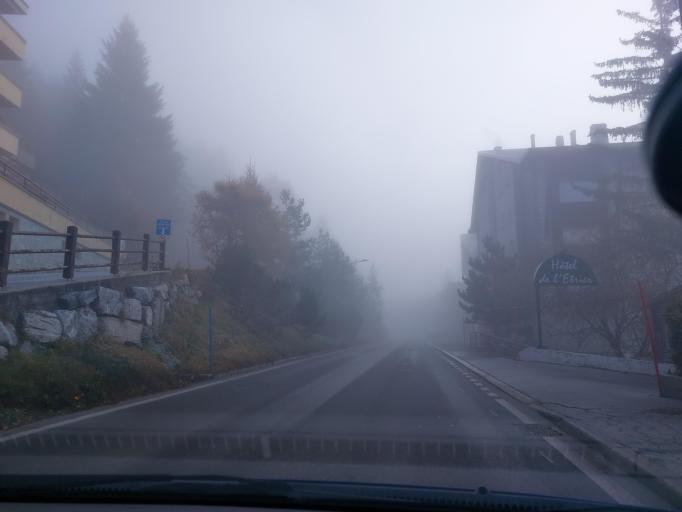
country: CH
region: Valais
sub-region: Sierre District
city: Montana
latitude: 46.3077
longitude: 7.4610
